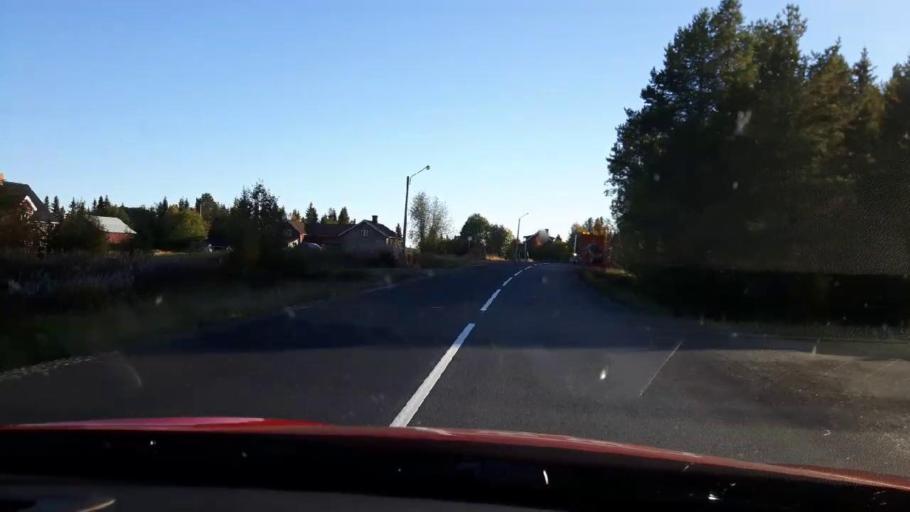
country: SE
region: Jaemtland
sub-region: OEstersunds Kommun
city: Lit
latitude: 63.5641
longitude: 14.9172
